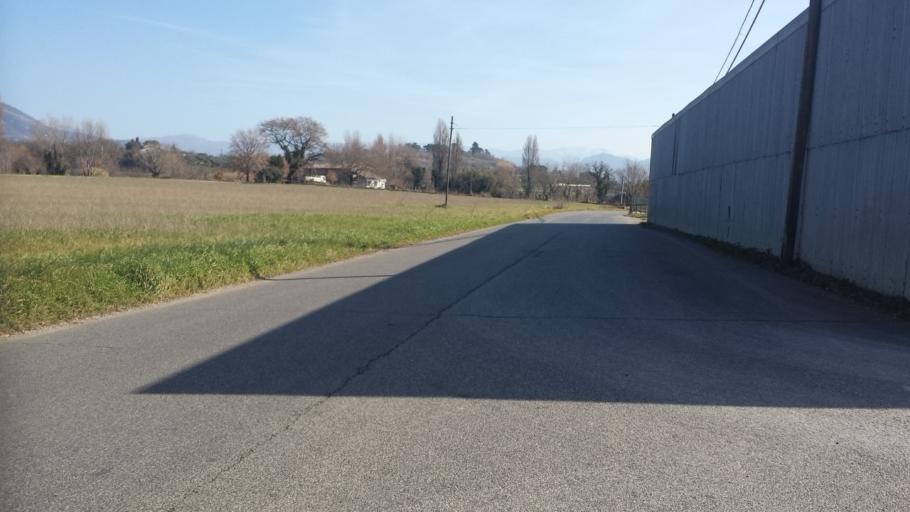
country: IT
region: Umbria
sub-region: Provincia di Terni
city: Terni
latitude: 42.5787
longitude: 12.5883
